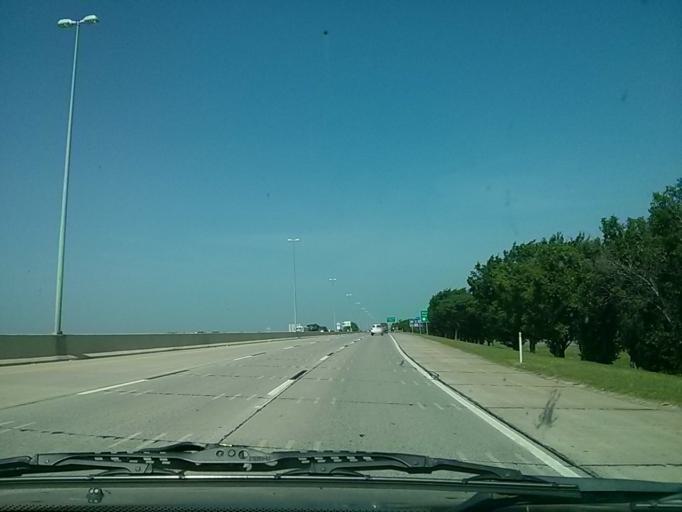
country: US
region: Oklahoma
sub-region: Tulsa County
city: Jenks
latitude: 36.0168
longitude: -95.9591
